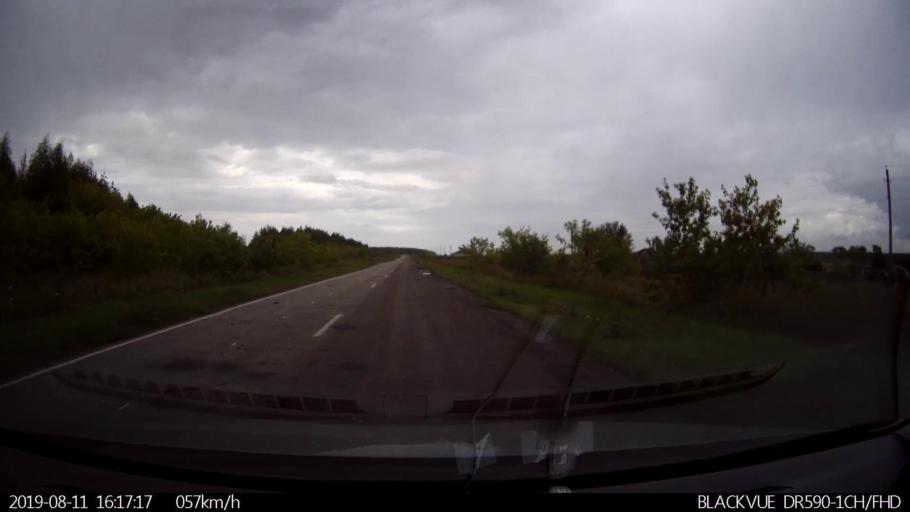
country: RU
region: Ulyanovsk
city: Mayna
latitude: 54.0474
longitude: 47.6170
